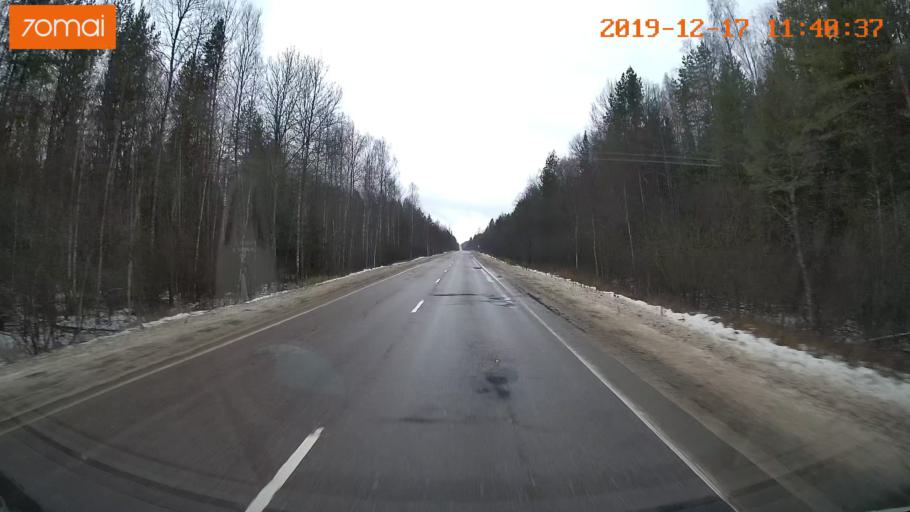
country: RU
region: Vladimir
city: Velikodvorskiy
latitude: 55.3148
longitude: 40.6738
